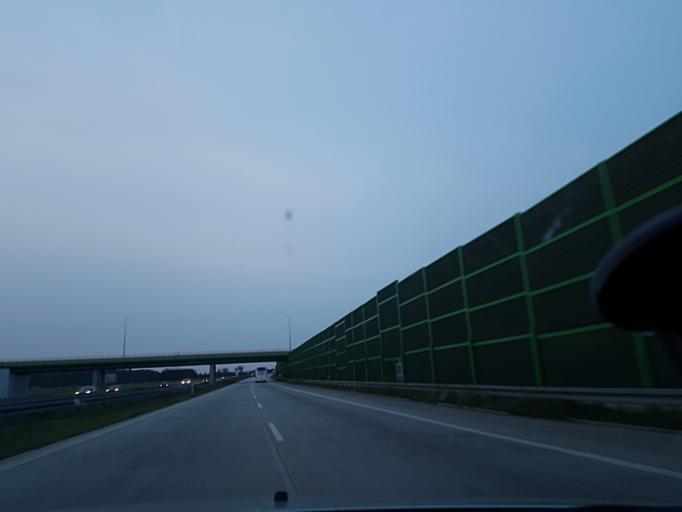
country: PL
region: Lodz Voivodeship
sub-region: Powiat zgierski
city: Strykow
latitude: 51.8681
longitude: 19.6548
